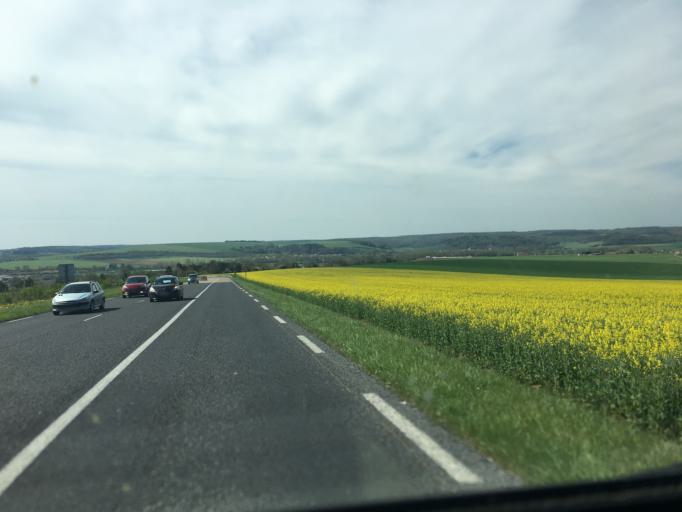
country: FR
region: Lorraine
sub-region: Departement de la Meuse
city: Saint-Mihiel
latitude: 48.8734
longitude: 5.5215
